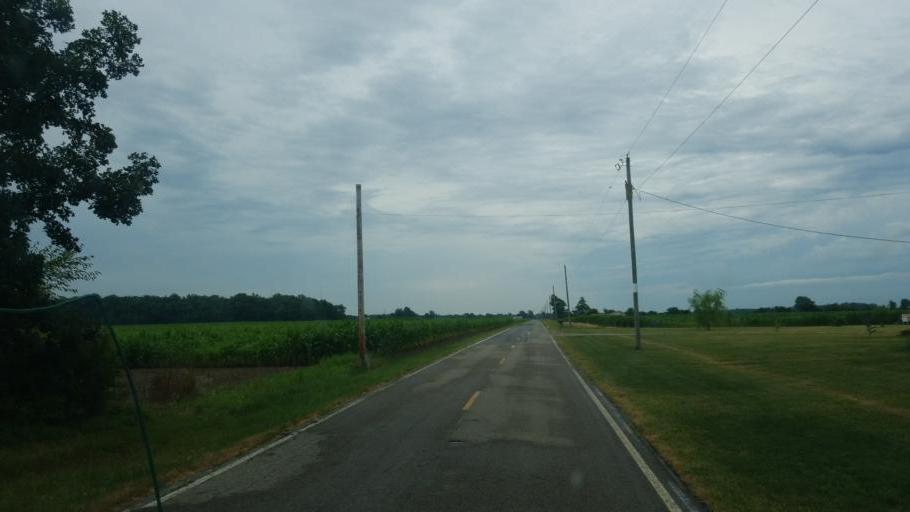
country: US
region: Ohio
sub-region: Defiance County
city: Hicksville
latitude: 41.2598
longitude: -84.6894
